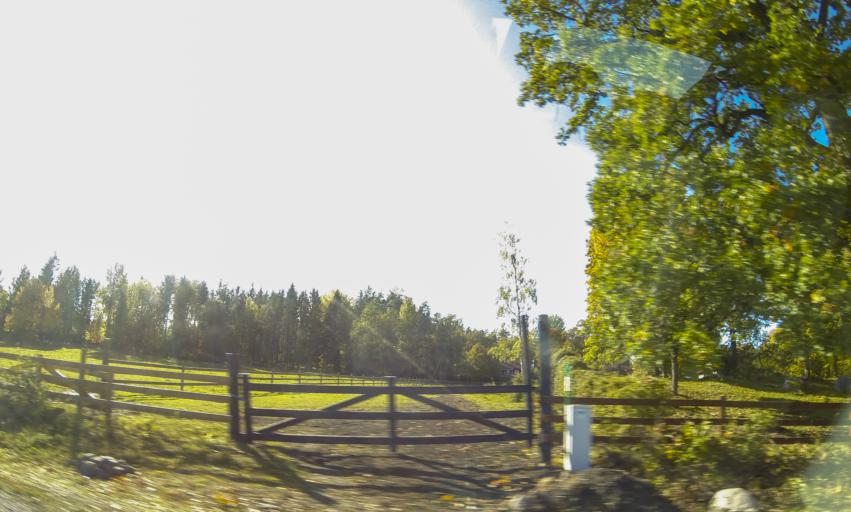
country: SE
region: Soedermanland
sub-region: Eskilstuna Kommun
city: Kvicksund
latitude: 59.5196
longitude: 16.3345
